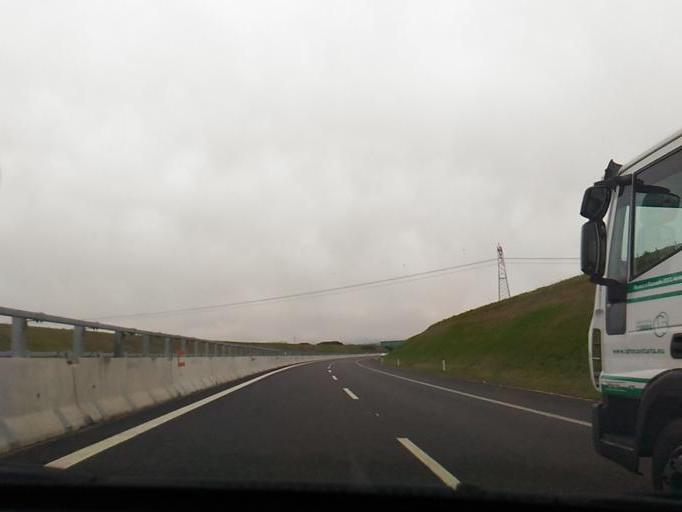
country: IT
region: Lombardy
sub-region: Provincia di Varese
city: Cislago
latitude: 45.6721
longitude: 8.9727
